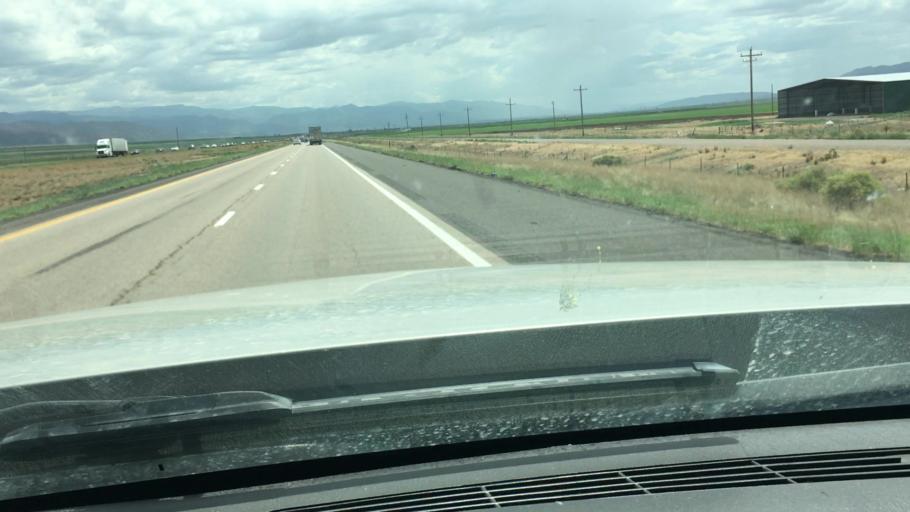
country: US
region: Utah
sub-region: Beaver County
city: Beaver
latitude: 38.0518
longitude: -112.6997
